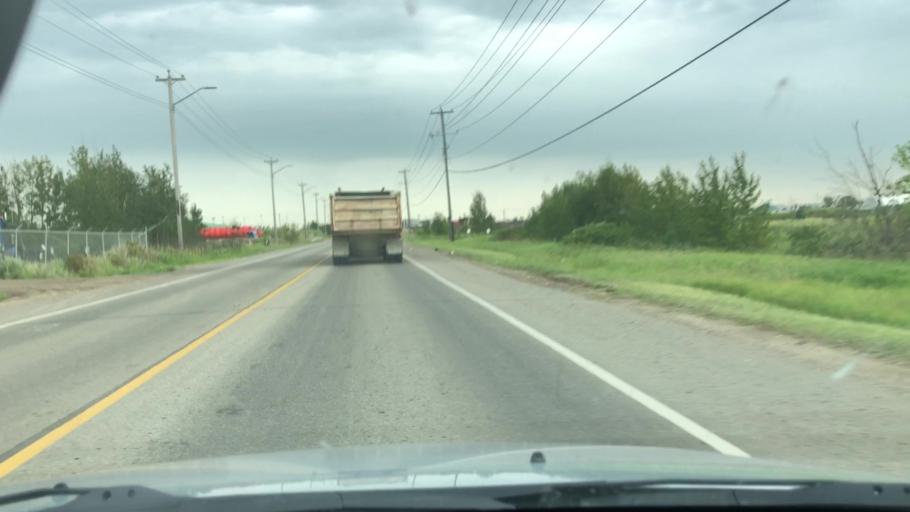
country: CA
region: Alberta
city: Sherwood Park
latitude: 53.5234
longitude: -113.3939
